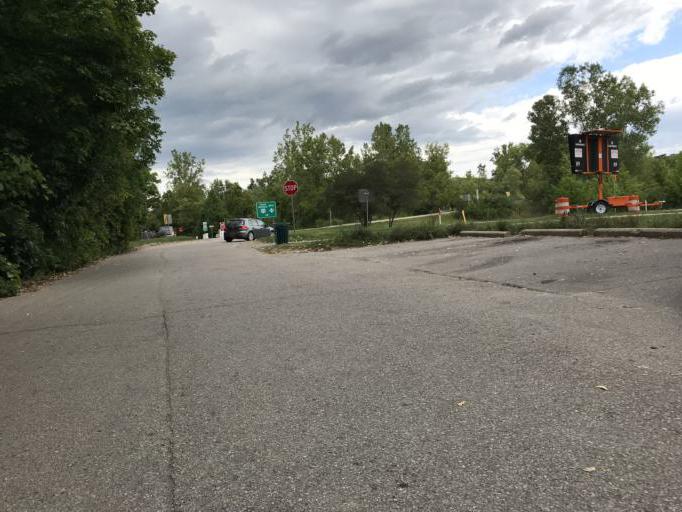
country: US
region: Michigan
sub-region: Washtenaw County
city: Ann Arbor
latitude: 42.3039
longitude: -83.7465
